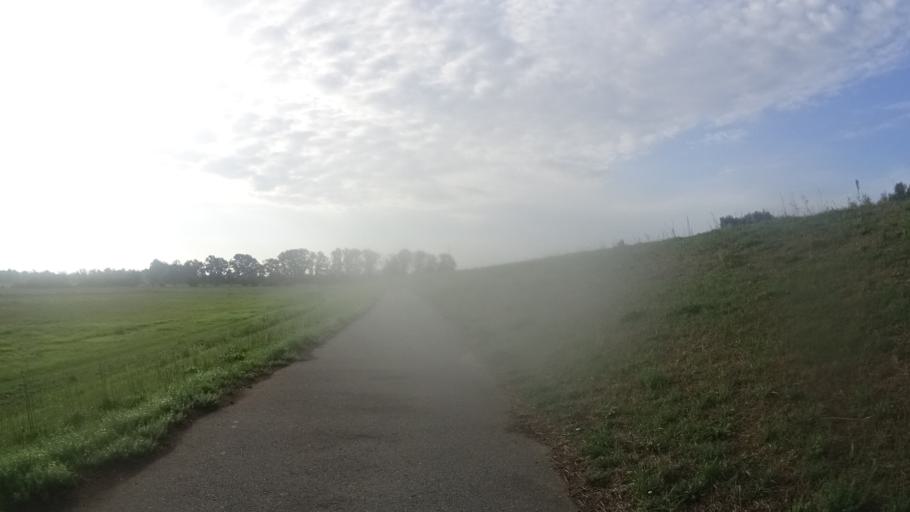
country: DE
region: Brandenburg
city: Lanz
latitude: 53.0484
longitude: 11.5720
